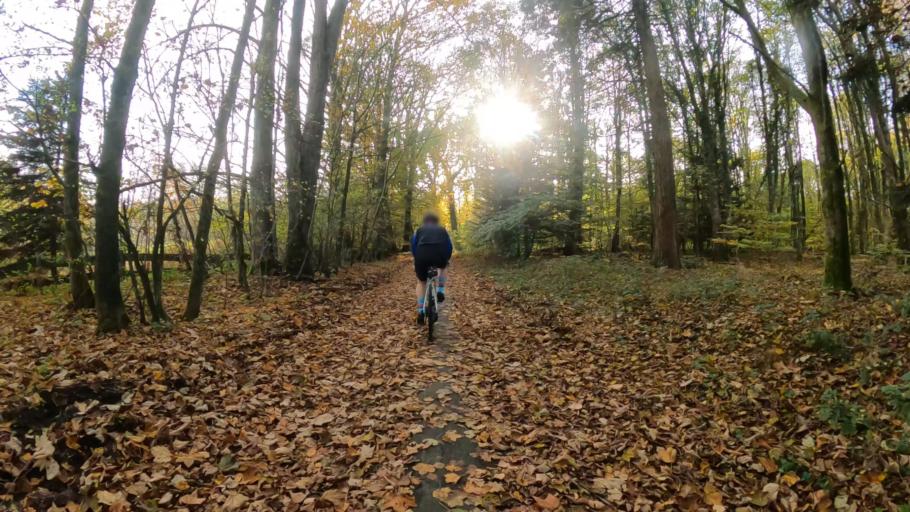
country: DE
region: Lower Saxony
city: Buchholz in der Nordheide
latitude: 53.4047
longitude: 9.8512
